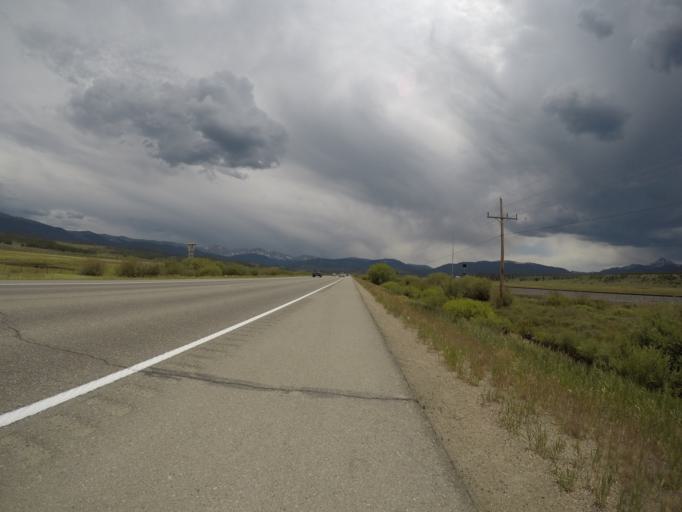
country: US
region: Colorado
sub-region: Grand County
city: Fraser
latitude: 39.9722
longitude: -105.8256
